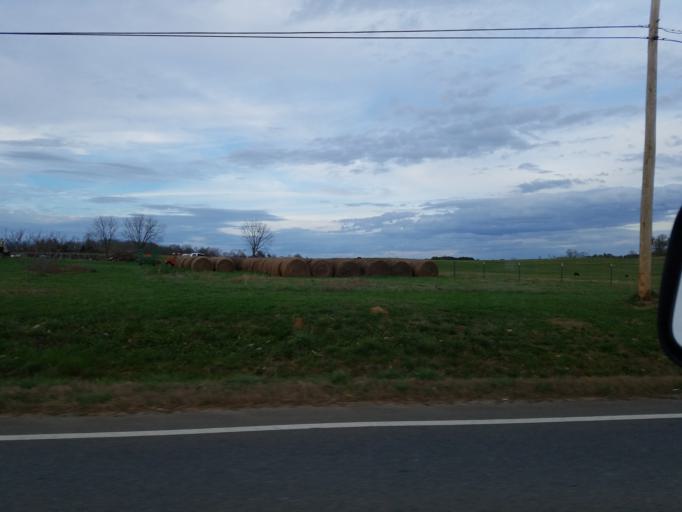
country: US
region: Georgia
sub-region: Gordon County
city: Calhoun
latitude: 34.4493
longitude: -84.8610
